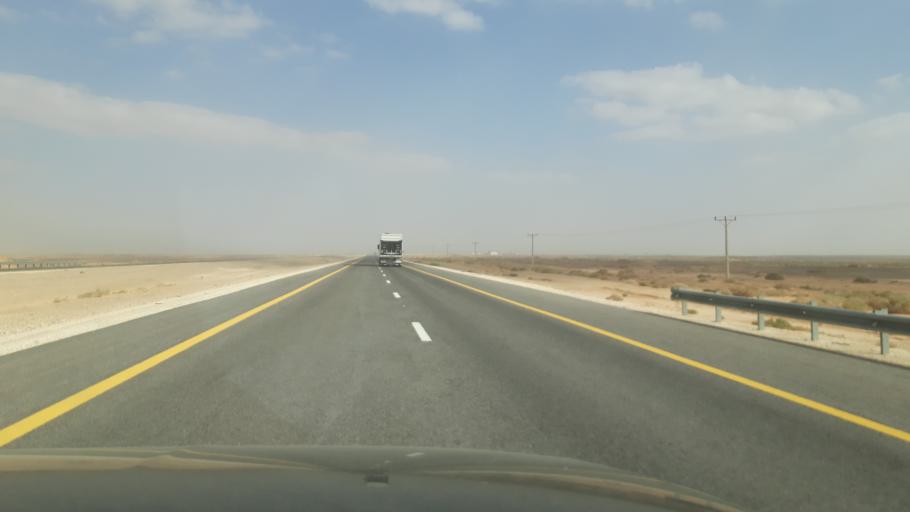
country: JO
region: Amman
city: Al Azraq ash Shamali
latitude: 31.7185
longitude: 36.8467
